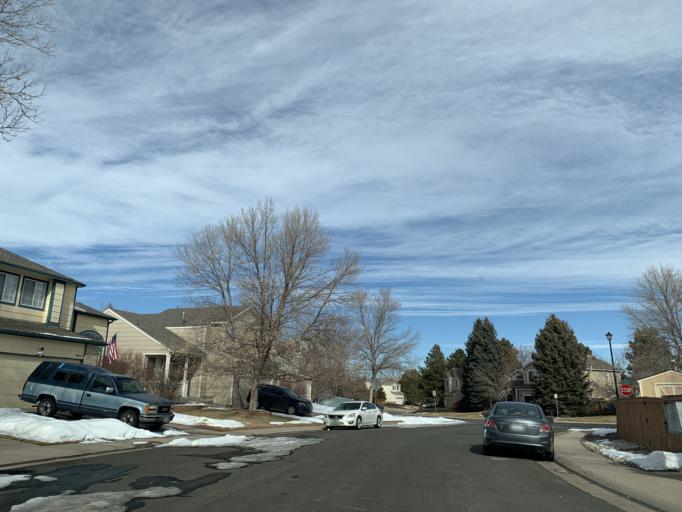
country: US
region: Colorado
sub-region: Douglas County
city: Carriage Club
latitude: 39.5405
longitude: -104.9298
